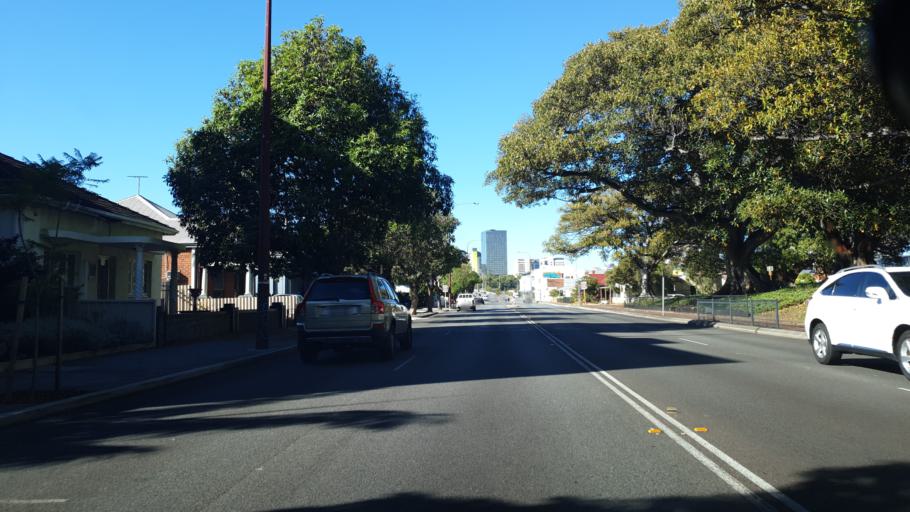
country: AU
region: Western Australia
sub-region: Cambridge
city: Perth
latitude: -31.9466
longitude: 115.8715
